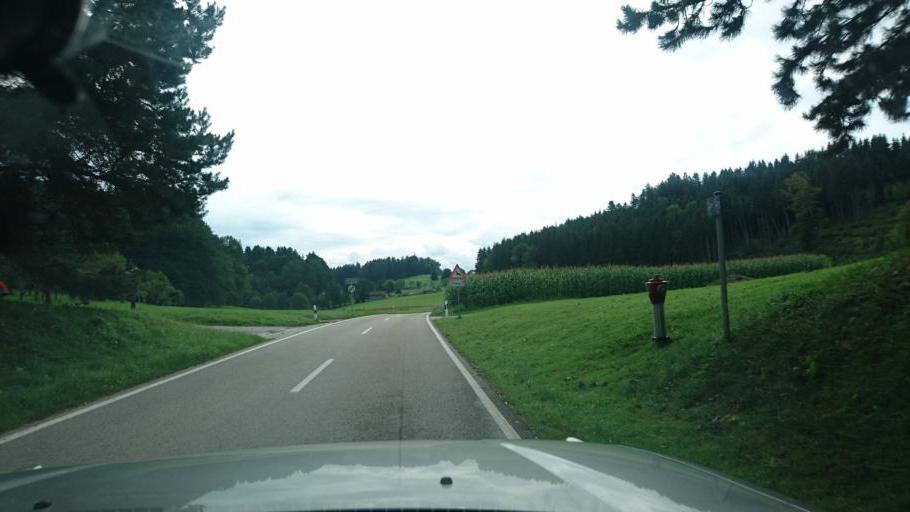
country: DE
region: Bavaria
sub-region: Upper Bavaria
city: Grabenstatt
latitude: 47.8337
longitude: 12.5643
